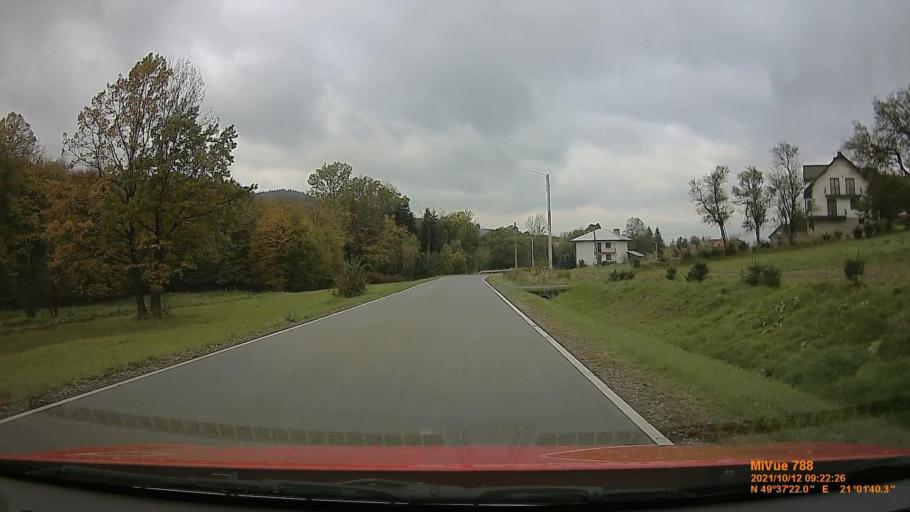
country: PL
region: Lesser Poland Voivodeship
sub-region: Powiat gorlicki
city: Ropa
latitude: 49.6228
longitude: 21.0277
